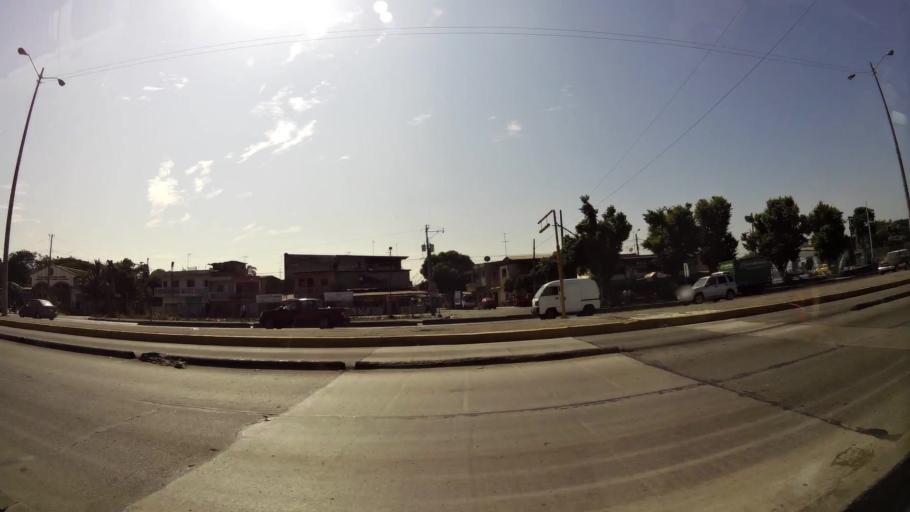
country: EC
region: Guayas
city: Guayaquil
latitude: -2.1131
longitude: -79.9334
